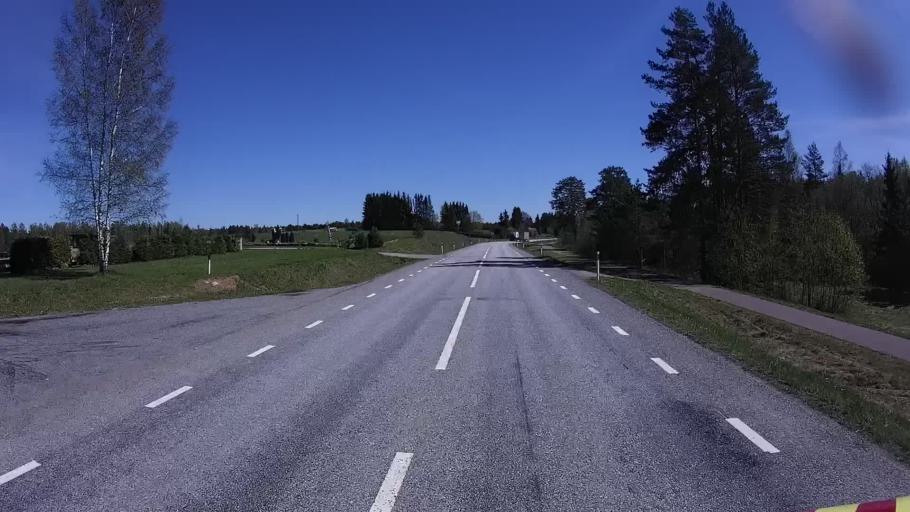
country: EE
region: Harju
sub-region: Kuusalu vald
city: Kuusalu
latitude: 59.2611
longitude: 25.6587
